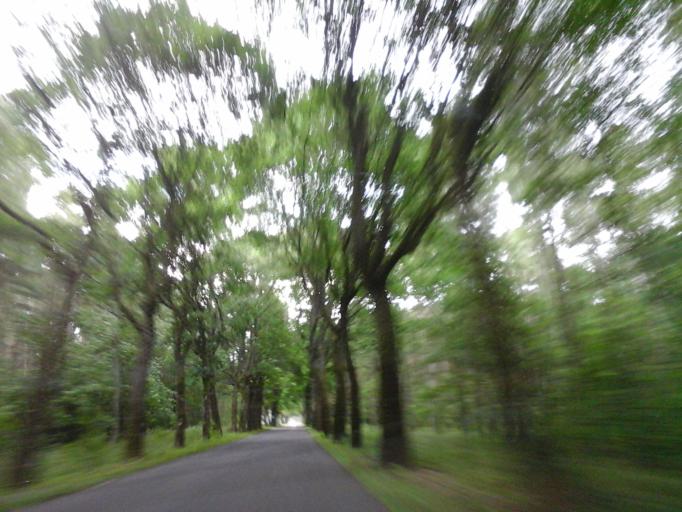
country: PL
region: West Pomeranian Voivodeship
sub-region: Powiat choszczenski
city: Drawno
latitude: 53.1976
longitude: 15.8278
